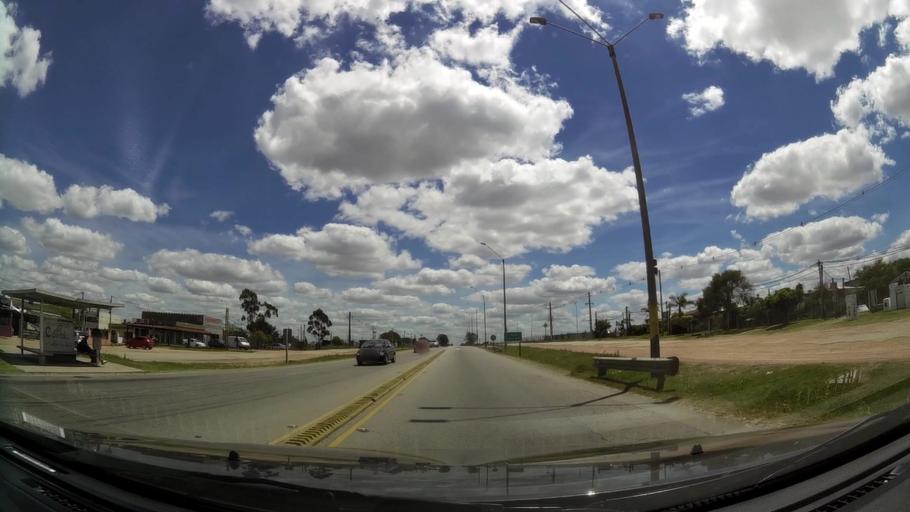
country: UY
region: Canelones
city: Colonia Nicolich
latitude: -34.8180
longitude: -56.0080
